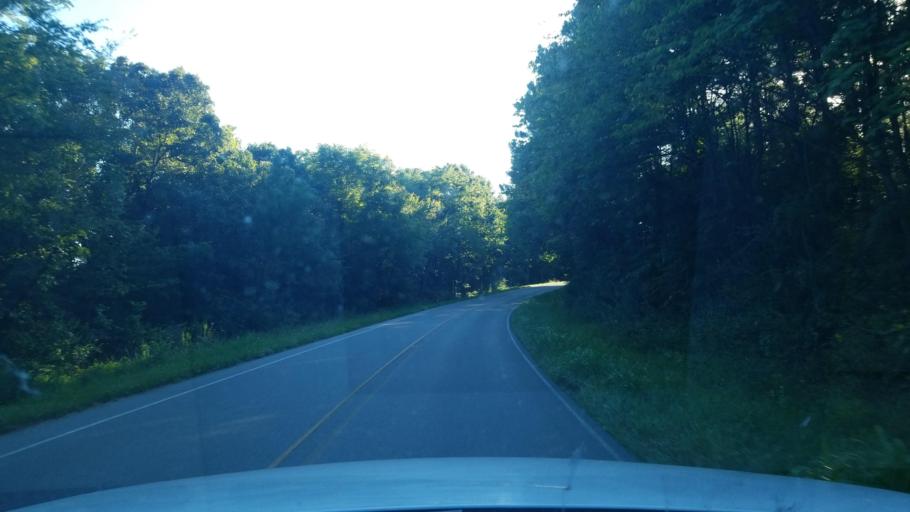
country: US
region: Illinois
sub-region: Hardin County
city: Elizabethtown
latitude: 37.5785
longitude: -88.3753
